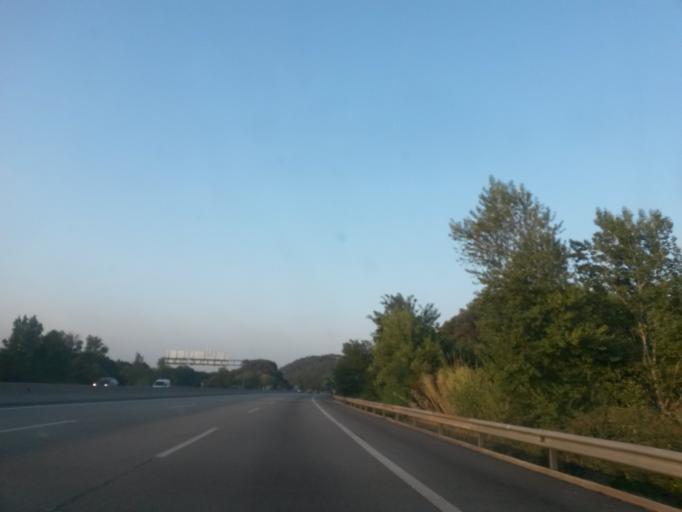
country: ES
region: Catalonia
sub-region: Provincia de Barcelona
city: Sant Celoni
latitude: 41.6820
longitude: 2.4927
